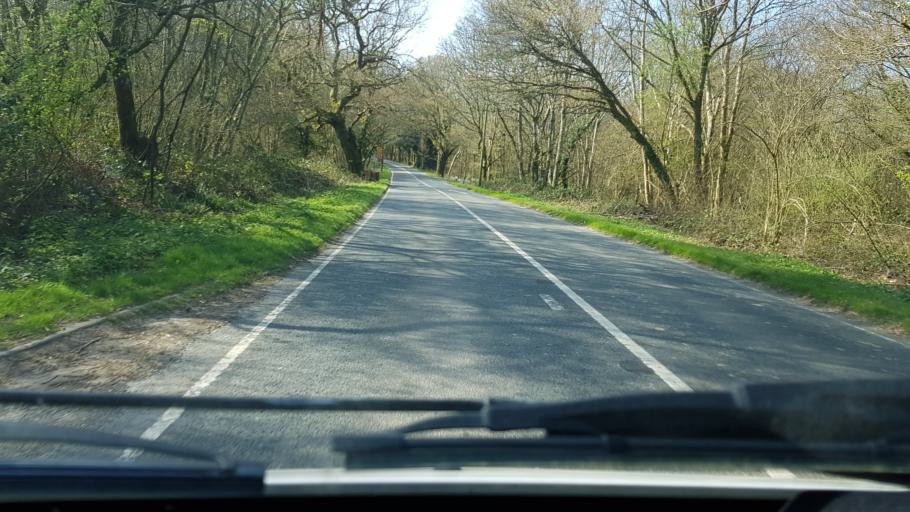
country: GB
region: England
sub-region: West Sussex
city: Fernhurst
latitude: 51.0304
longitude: -0.7327
